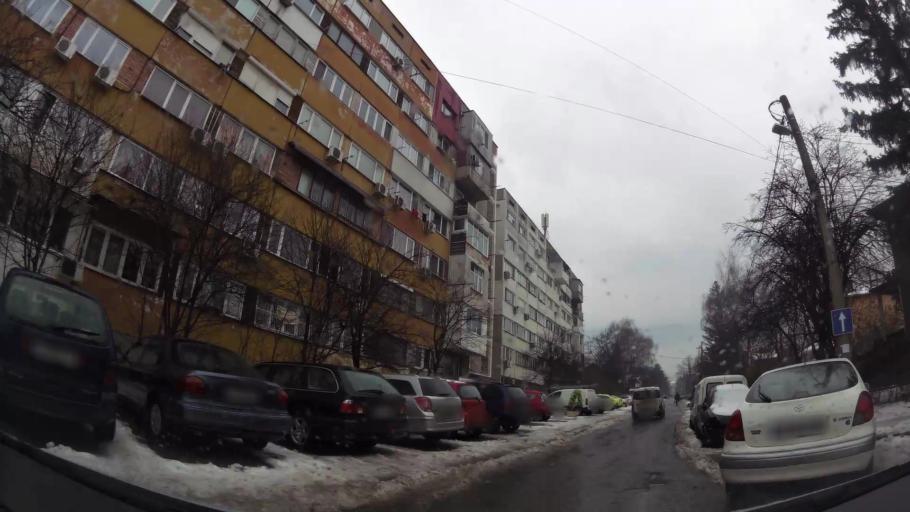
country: BG
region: Sofia-Capital
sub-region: Stolichna Obshtina
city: Sofia
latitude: 42.6652
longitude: 23.2693
